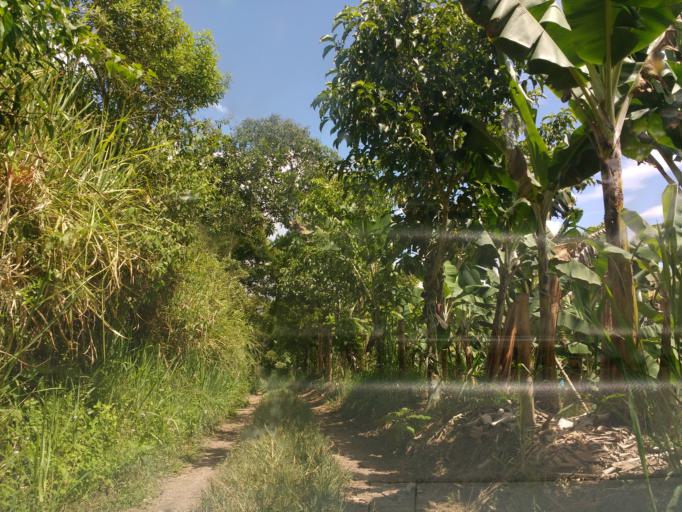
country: CO
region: Valle del Cauca
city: Alcala
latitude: 4.6768
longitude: -75.8091
